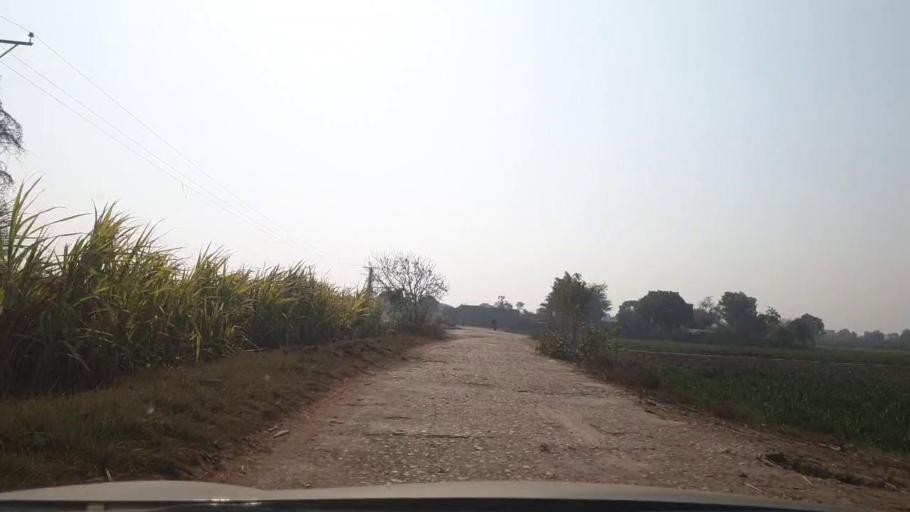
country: PK
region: Sindh
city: Tando Allahyar
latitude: 25.4918
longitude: 68.7557
